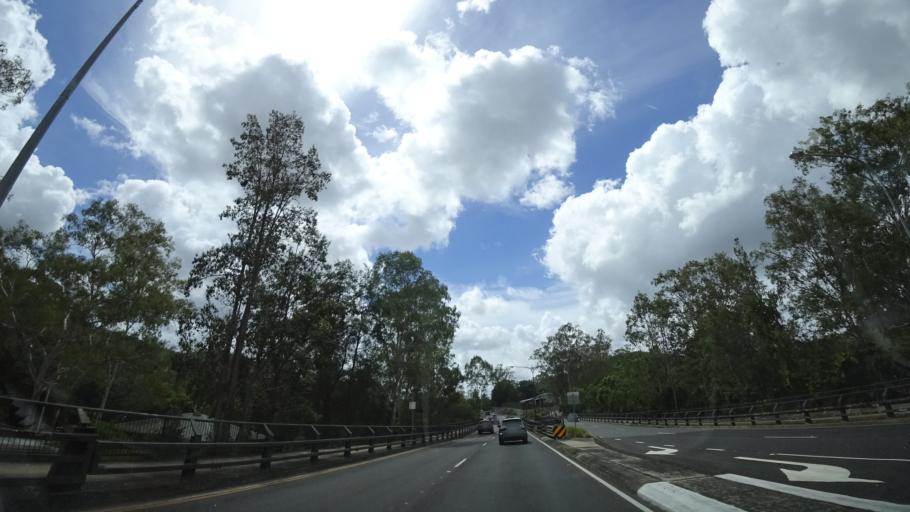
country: AU
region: Queensland
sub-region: Brisbane
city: Everton Park
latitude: -27.4450
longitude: 152.9546
